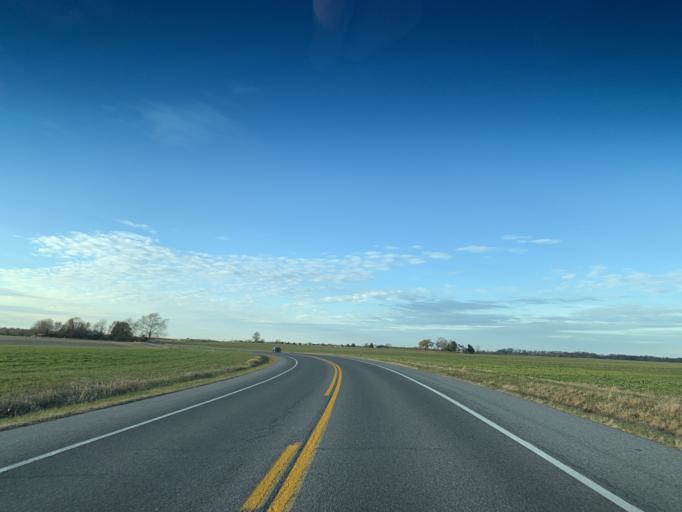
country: US
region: Maryland
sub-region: Kent County
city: Chestertown
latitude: 39.2463
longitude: -76.0714
